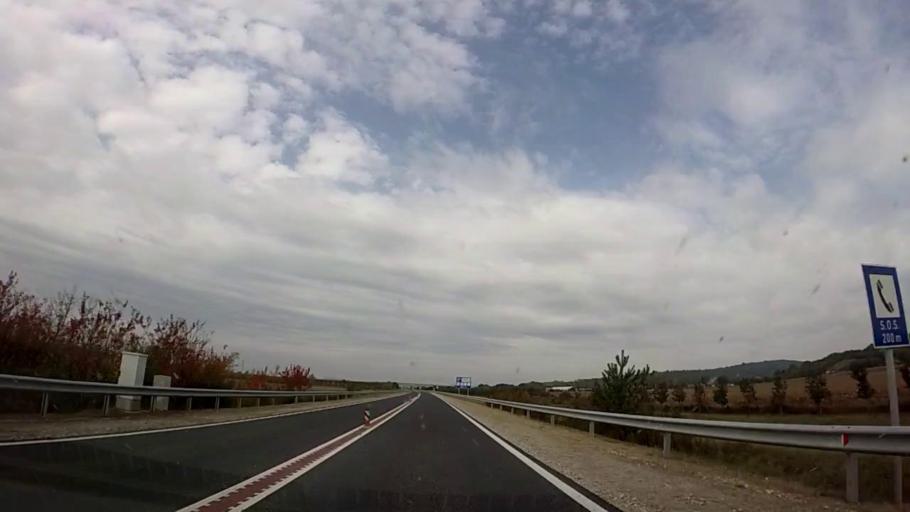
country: HR
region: Medimurska
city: Domasinec
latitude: 46.4983
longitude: 16.6224
